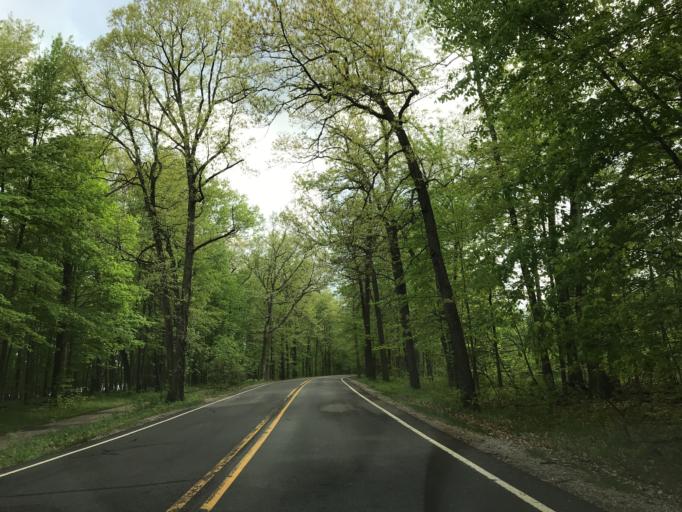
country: US
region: Michigan
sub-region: Oakland County
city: South Lyon
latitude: 42.5339
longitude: -83.6610
